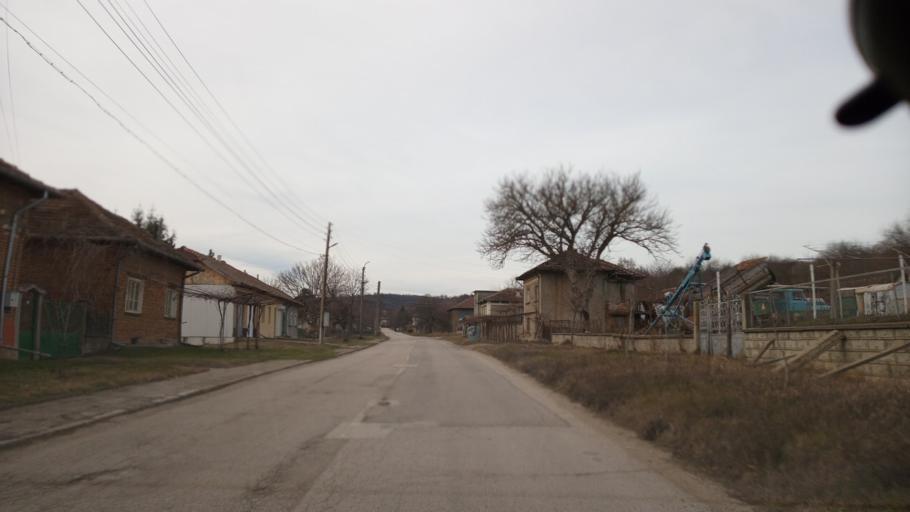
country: BG
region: Pleven
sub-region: Obshtina Belene
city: Belene
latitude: 43.6099
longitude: 25.0111
